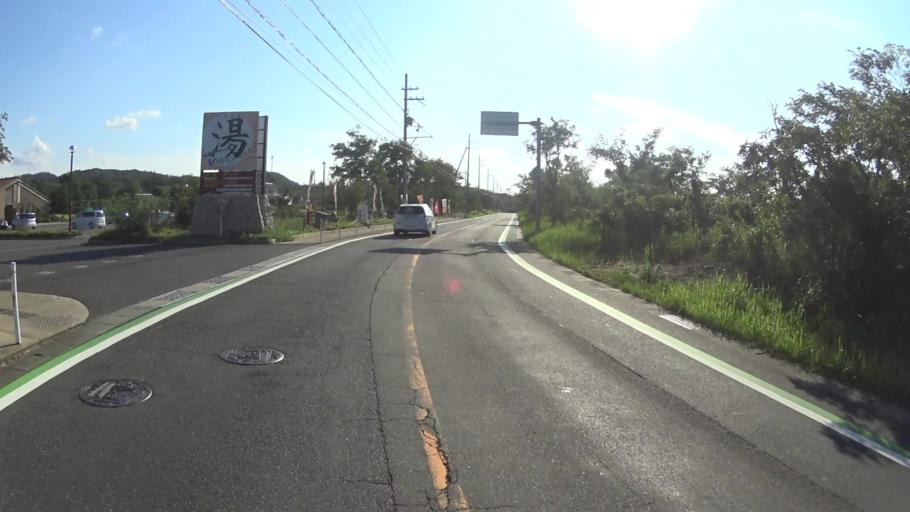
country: JP
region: Hyogo
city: Toyooka
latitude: 35.6590
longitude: 134.9633
